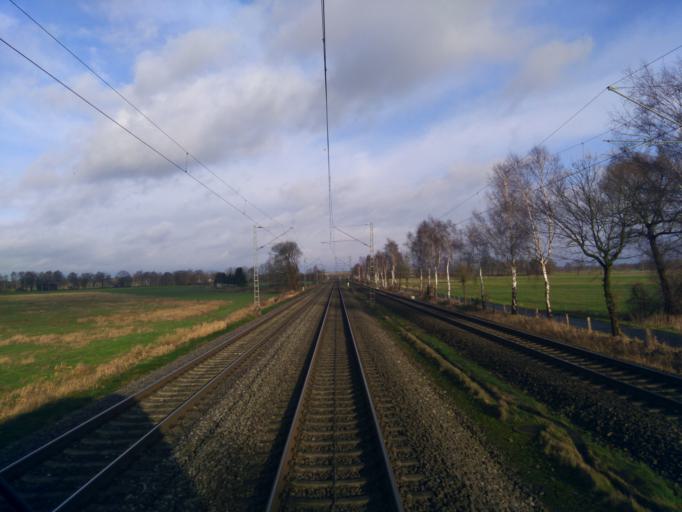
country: DE
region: Lower Saxony
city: Scheessel
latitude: 53.1770
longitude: 9.5120
